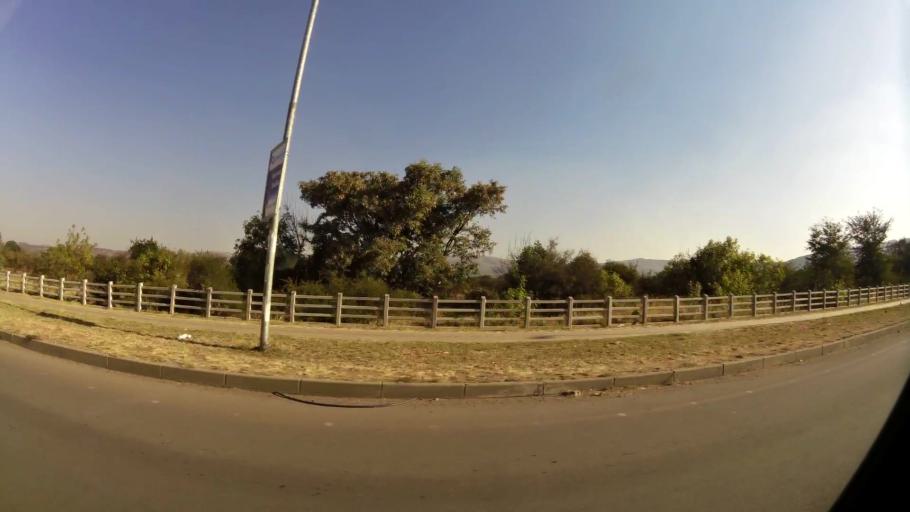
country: ZA
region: North-West
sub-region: Bojanala Platinum District Municipality
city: Rustenburg
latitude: -25.6605
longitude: 27.2291
